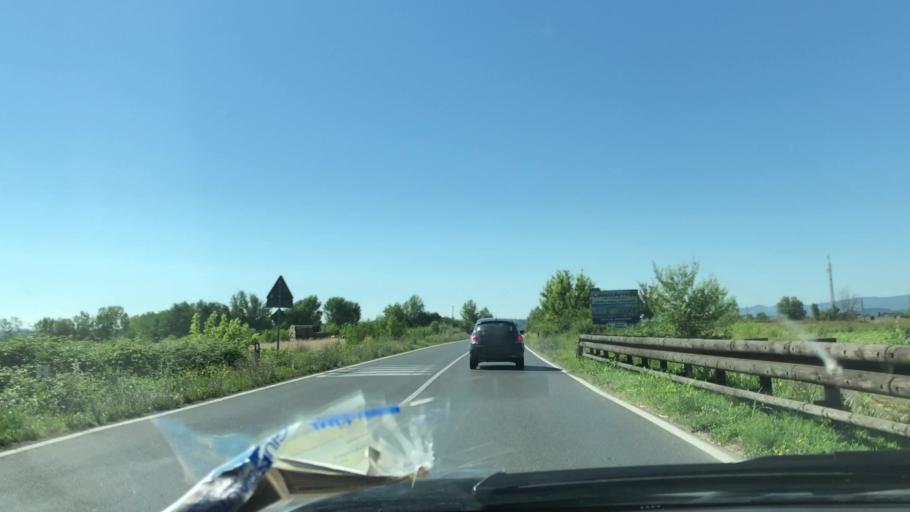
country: IT
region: Tuscany
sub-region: Province of Pisa
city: Forcoli
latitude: 43.5991
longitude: 10.6957
